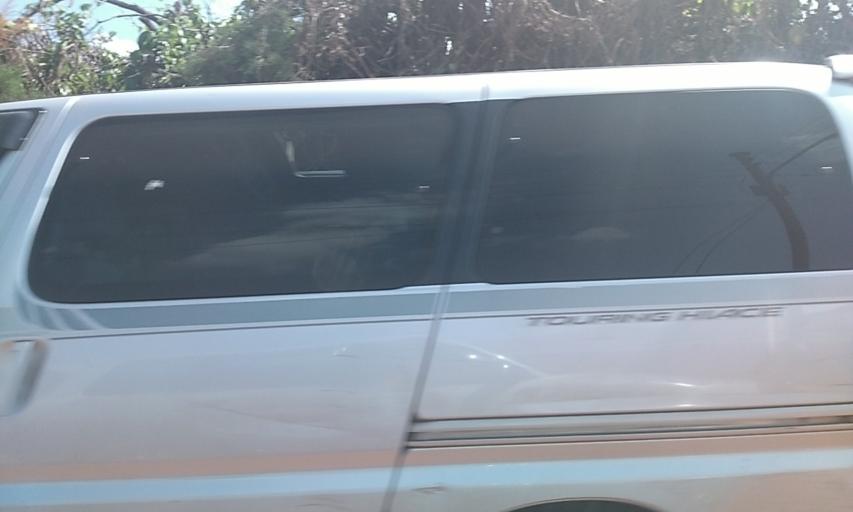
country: UG
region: Central Region
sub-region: Wakiso District
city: Kireka
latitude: 0.3471
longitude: 32.6161
